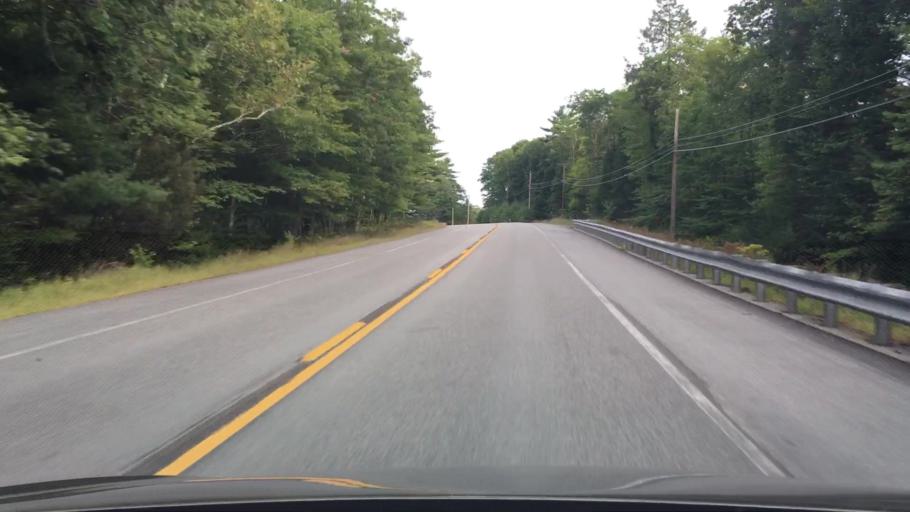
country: US
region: Maine
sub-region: Cumberland County
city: Bridgton
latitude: 44.0666
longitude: -70.7598
